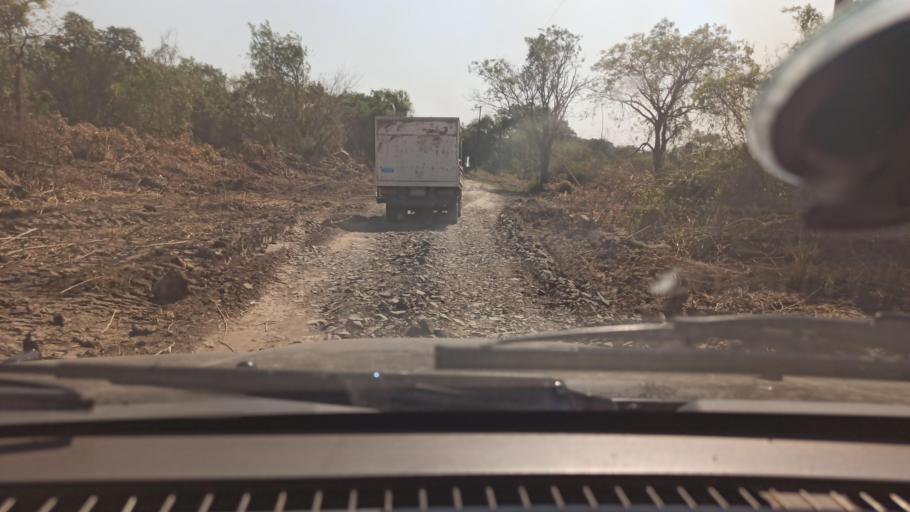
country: PY
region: Asuncion
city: Asuncion
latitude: -25.3408
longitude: -57.6775
